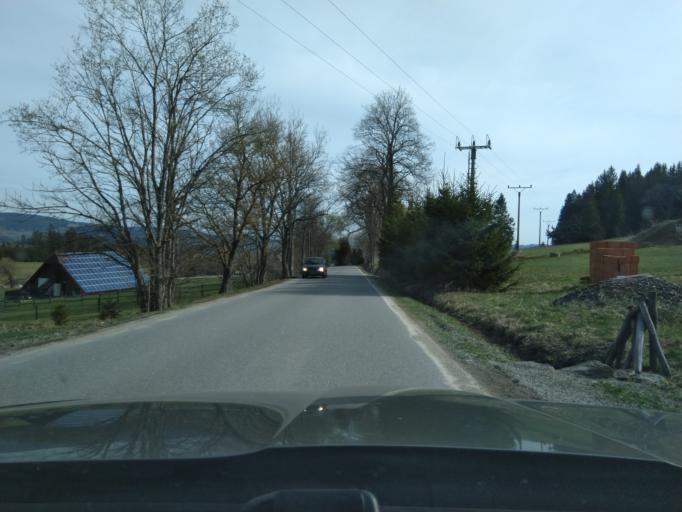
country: CZ
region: Jihocesky
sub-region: Okres Prachatice
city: Stachy
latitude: 49.0738
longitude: 13.6523
